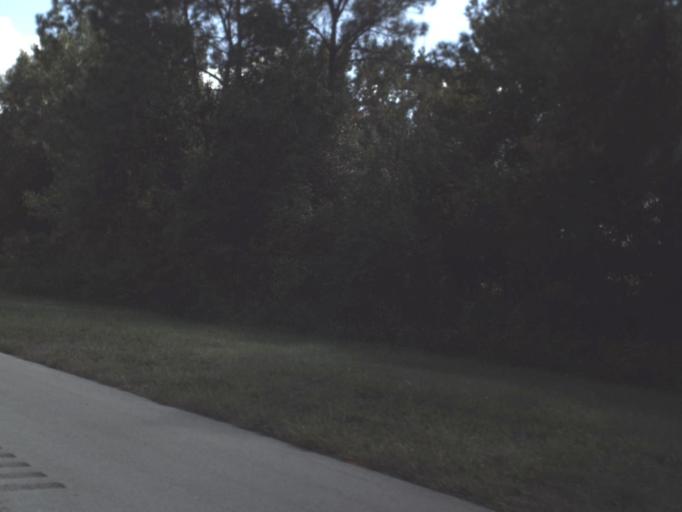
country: US
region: Florida
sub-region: Osceola County
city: Saint Cloud
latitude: 28.0575
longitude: -81.2300
